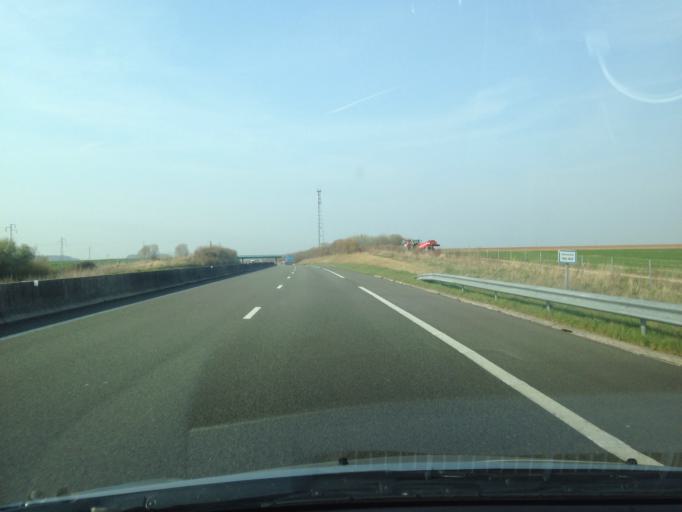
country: FR
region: Picardie
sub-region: Departement de la Somme
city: Sailly-Flibeaucourt
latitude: 50.1996
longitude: 1.7590
